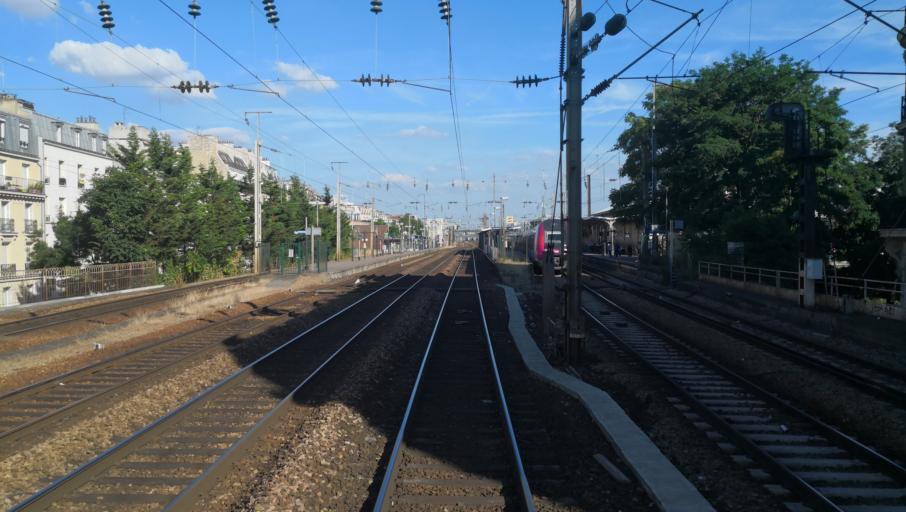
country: FR
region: Ile-de-France
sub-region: Departement des Hauts-de-Seine
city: Asnieres-sur-Seine
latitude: 48.9069
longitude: 2.2820
